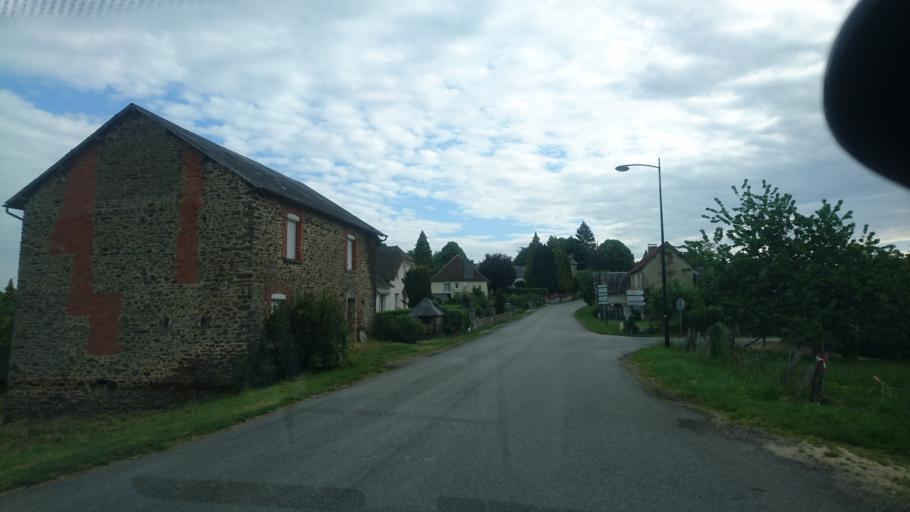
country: FR
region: Limousin
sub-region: Departement de la Haute-Vienne
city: Saint-Germain-les-Belles
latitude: 45.6196
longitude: 1.4996
